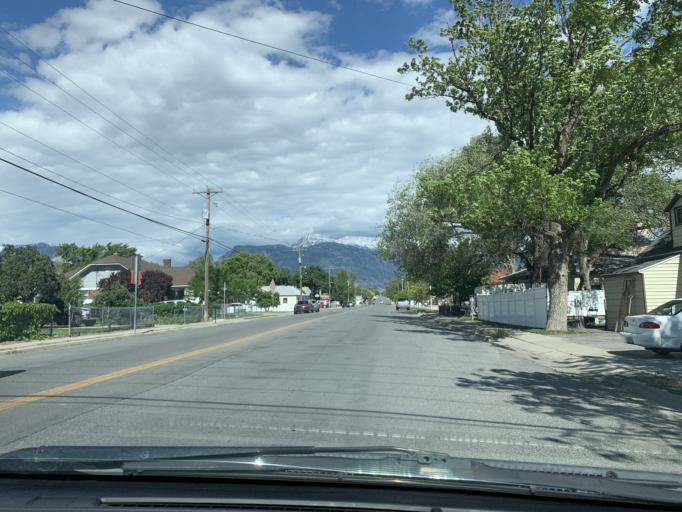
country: US
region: Utah
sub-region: Utah County
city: Lehi
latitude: 40.3989
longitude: -111.8433
